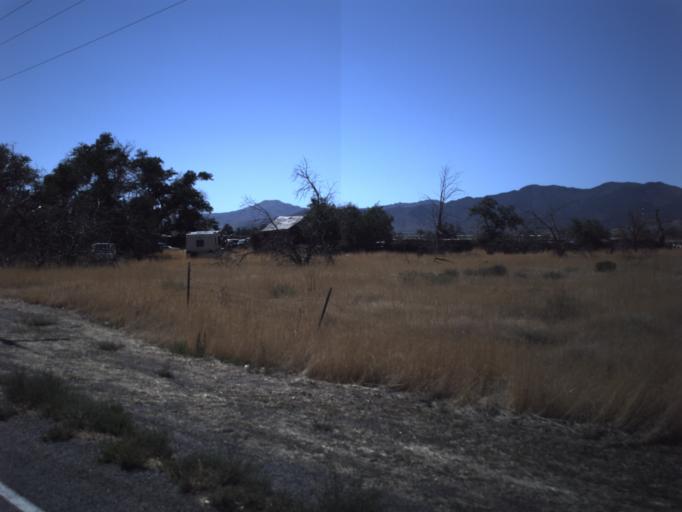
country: US
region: Utah
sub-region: Utah County
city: Genola
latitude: 39.9599
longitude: -111.9564
